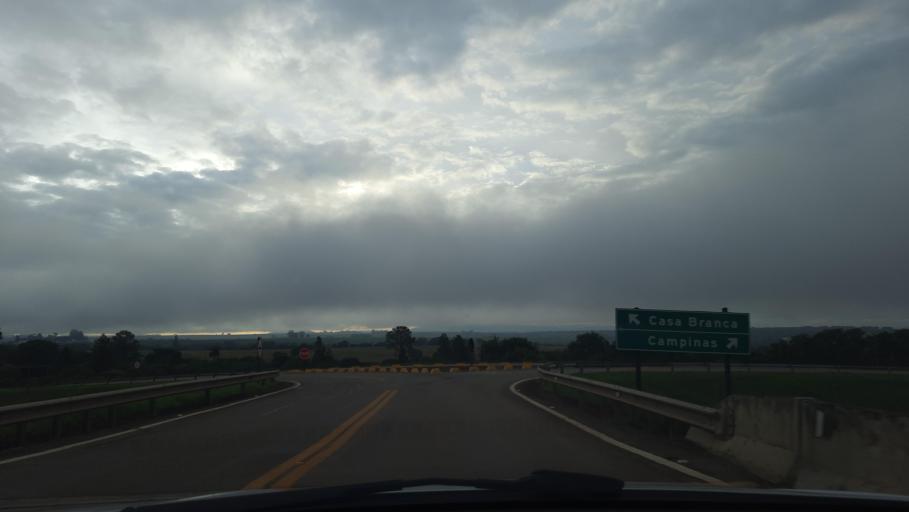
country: BR
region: Sao Paulo
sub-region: Casa Branca
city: Casa Branca
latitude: -21.7490
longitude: -47.0720
